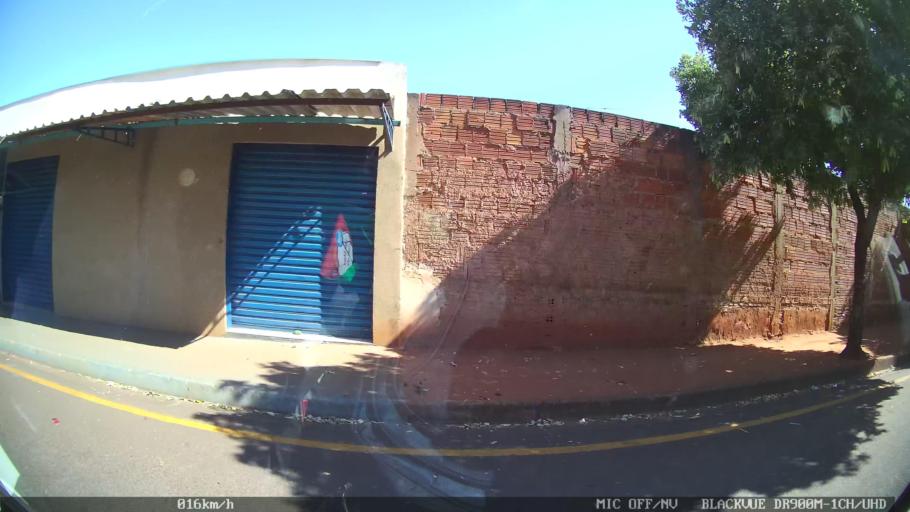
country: BR
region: Sao Paulo
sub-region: Sao Jose Do Rio Preto
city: Sao Jose do Rio Preto
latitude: -20.7508
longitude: -49.4071
